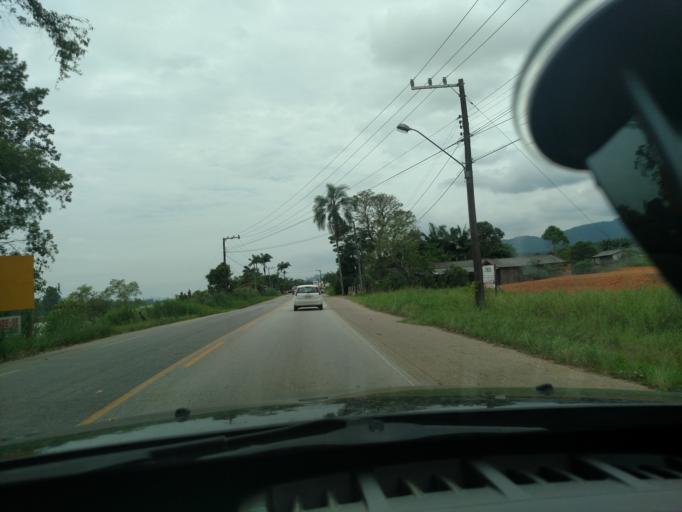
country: BR
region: Santa Catarina
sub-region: Gaspar
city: Gaspar
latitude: -26.9109
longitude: -48.8597
